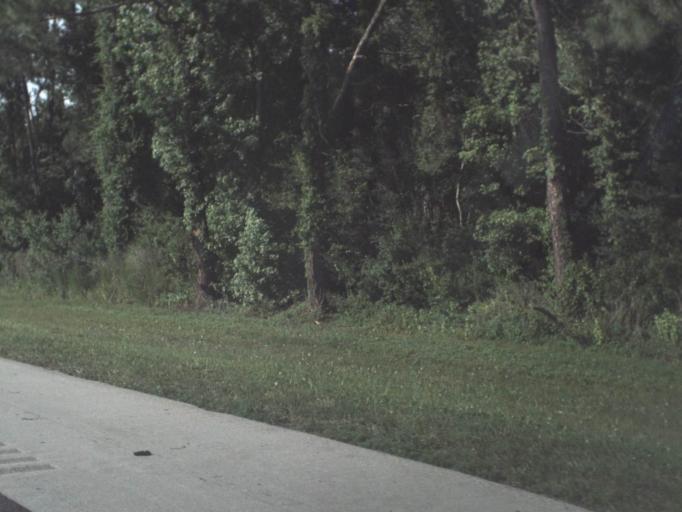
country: US
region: Florida
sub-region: Saint Johns County
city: Saint Augustine
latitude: 29.9088
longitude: -81.4092
